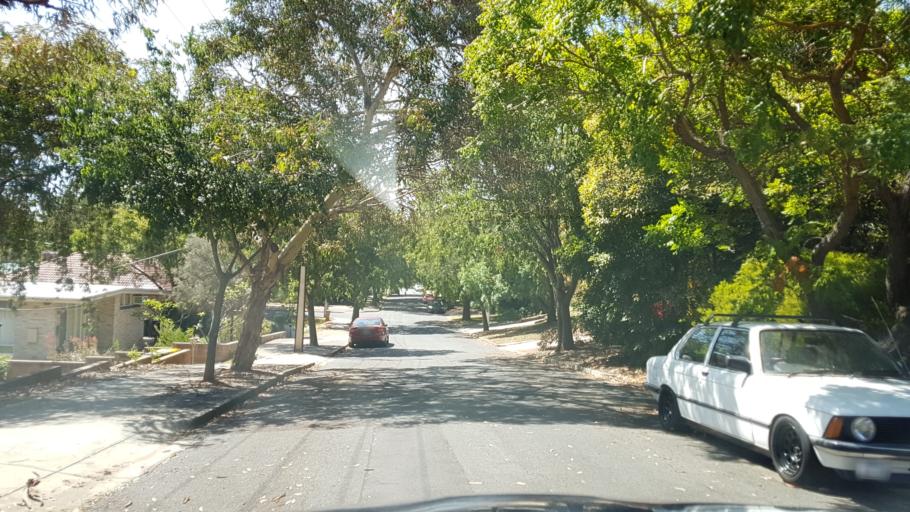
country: AU
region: South Australia
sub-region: Onkaparinga
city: Bedford Park
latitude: -35.0286
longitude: 138.5649
